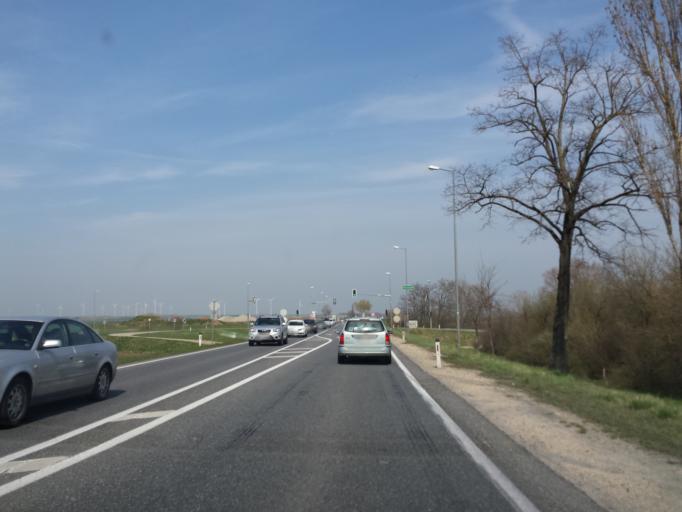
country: AT
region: Lower Austria
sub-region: Politischer Bezirk Mistelbach
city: Wilfersdorf
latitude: 48.5608
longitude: 16.6365
